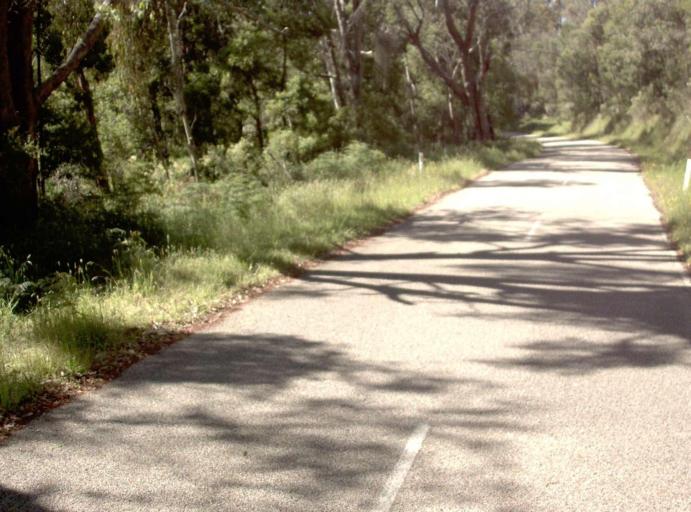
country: AU
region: New South Wales
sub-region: Bombala
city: Bombala
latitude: -37.3398
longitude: 148.6982
